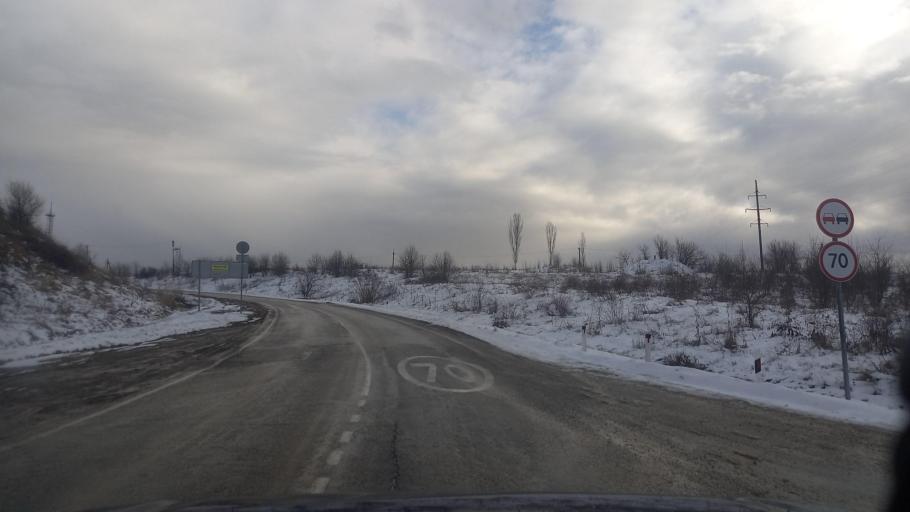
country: RU
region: Krasnodarskiy
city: Smolenskaya
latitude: 44.7722
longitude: 38.8180
